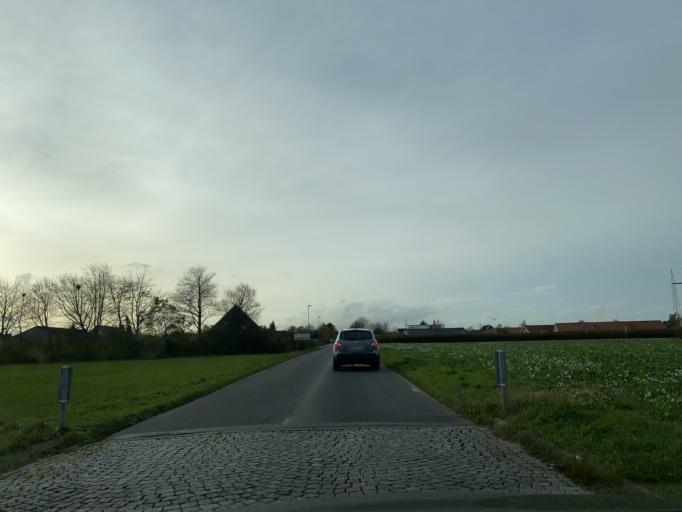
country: DK
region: Central Jutland
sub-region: Skanderborg Kommune
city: Skovby
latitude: 56.1593
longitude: 9.9602
